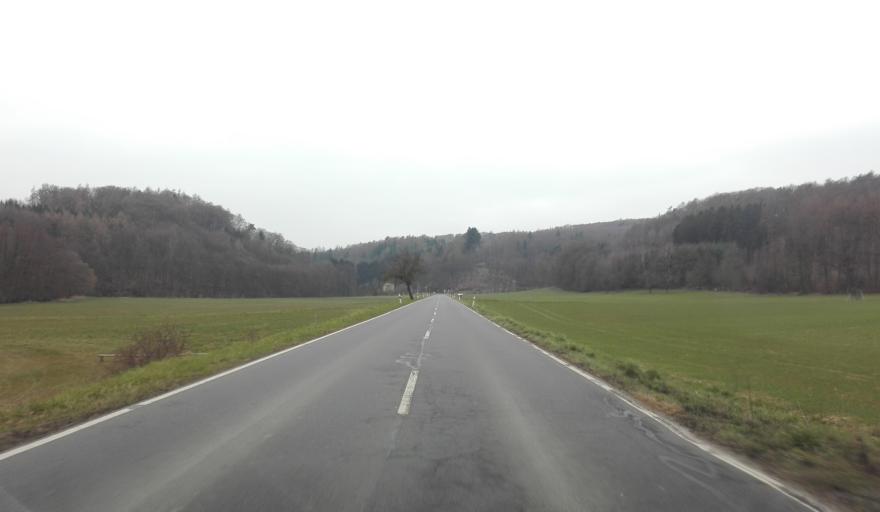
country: DE
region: Hesse
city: Lutzelbach
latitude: 49.7669
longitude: 8.7311
